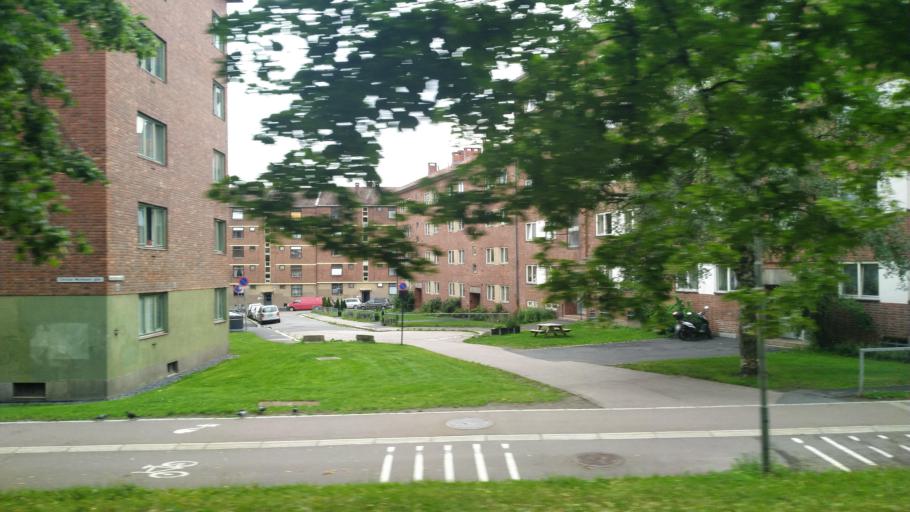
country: NO
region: Oslo
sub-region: Oslo
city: Oslo
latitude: 59.9304
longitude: 10.7666
